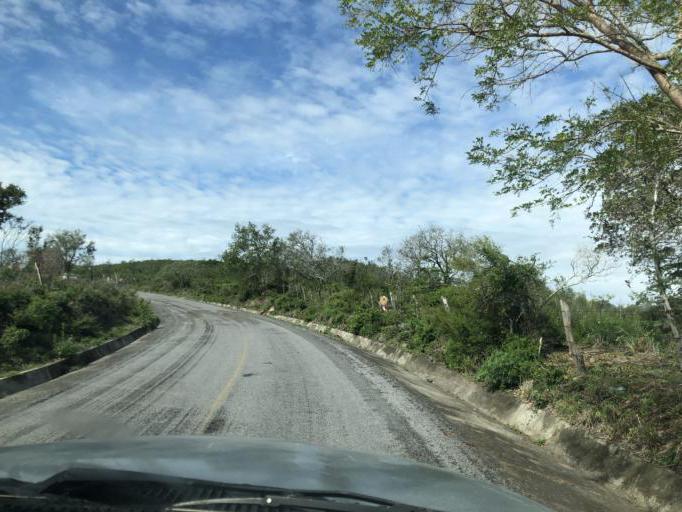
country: MX
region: Veracruz
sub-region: Juchique de Ferrer
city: Plan de las Hayas
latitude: 19.7813
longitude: -96.5558
